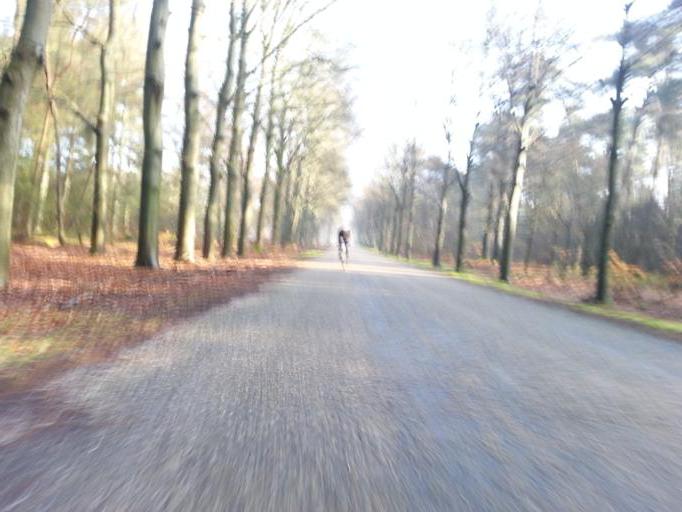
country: NL
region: Utrecht
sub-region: Gemeente Utrechtse Heuvelrug
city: Maarsbergen
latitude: 52.0457
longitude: 5.3908
